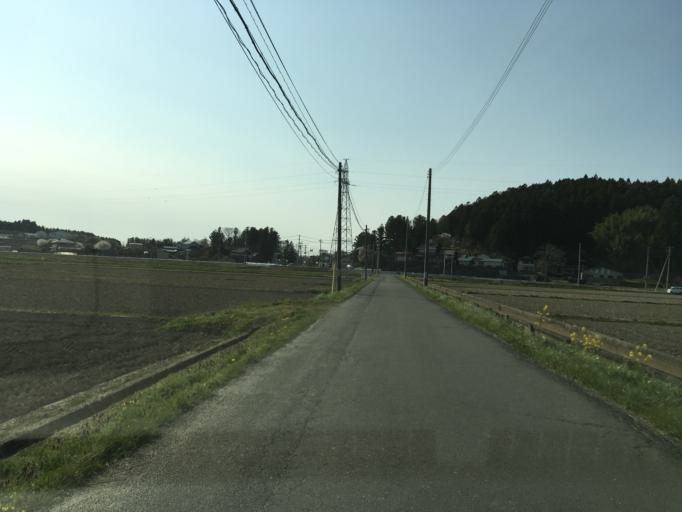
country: JP
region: Miyagi
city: Wakuya
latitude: 38.7288
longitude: 141.2897
